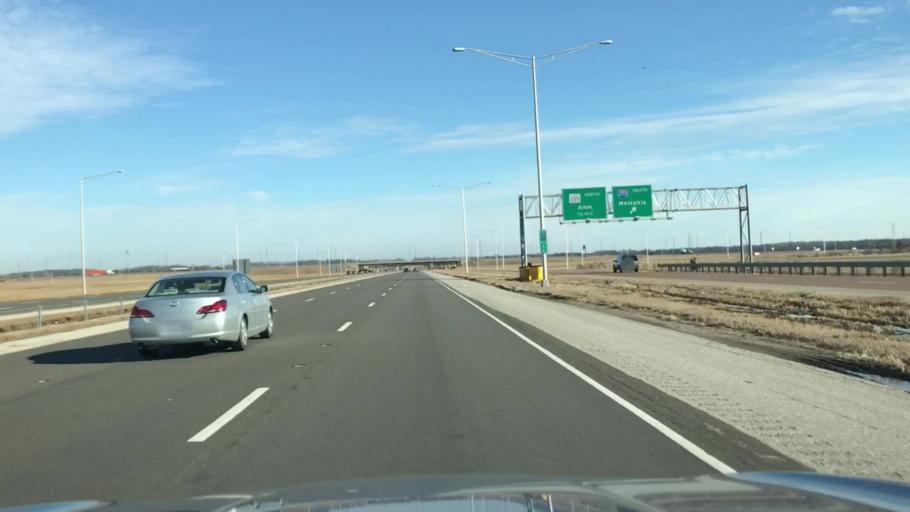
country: US
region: Illinois
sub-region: Madison County
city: Mitchell
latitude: 38.7574
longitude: -90.0518
